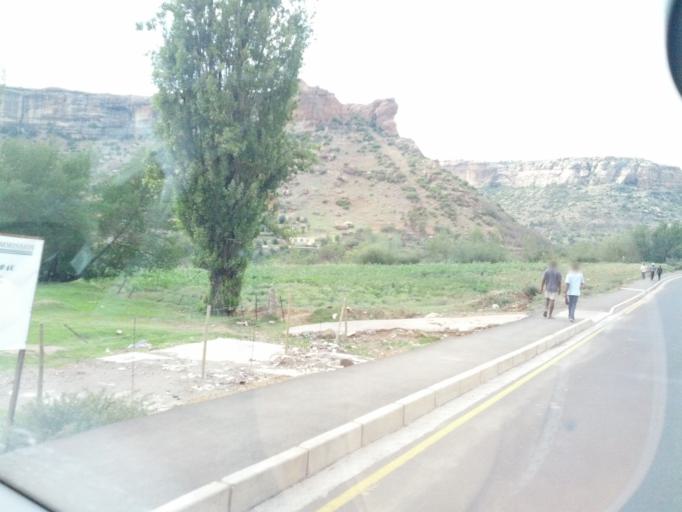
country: LS
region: Maseru
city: Nako
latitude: -29.4704
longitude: 27.7385
